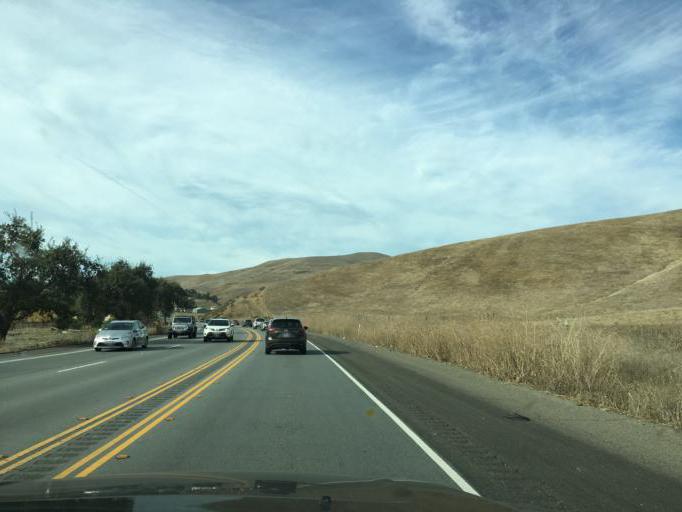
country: US
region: California
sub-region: San Benito County
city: Hollister
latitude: 36.9682
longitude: -121.4126
